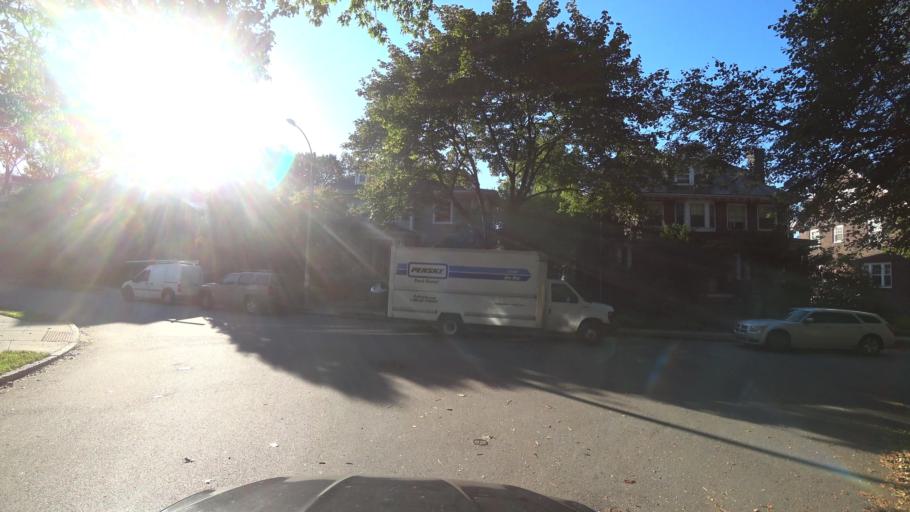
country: US
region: Massachusetts
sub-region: Norfolk County
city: Brookline
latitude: 42.3392
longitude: -71.1414
